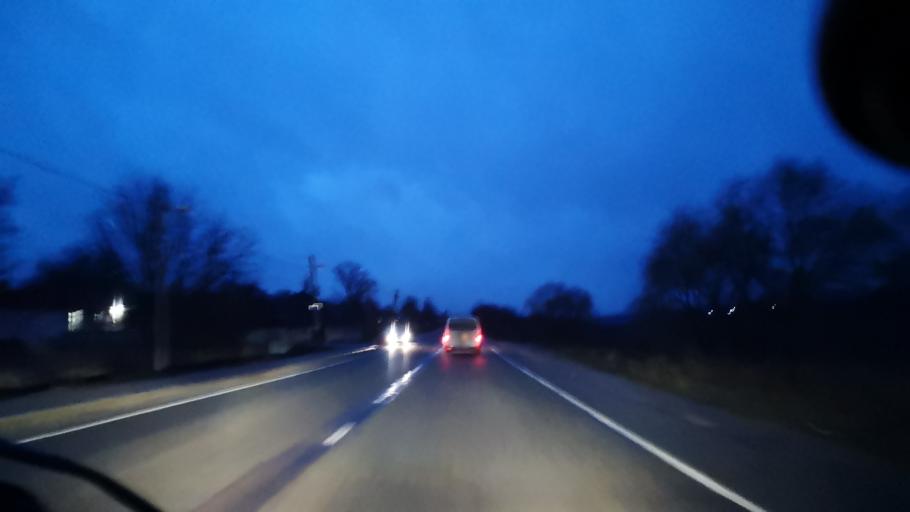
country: MD
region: Orhei
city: Orhei
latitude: 47.4476
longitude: 28.7930
